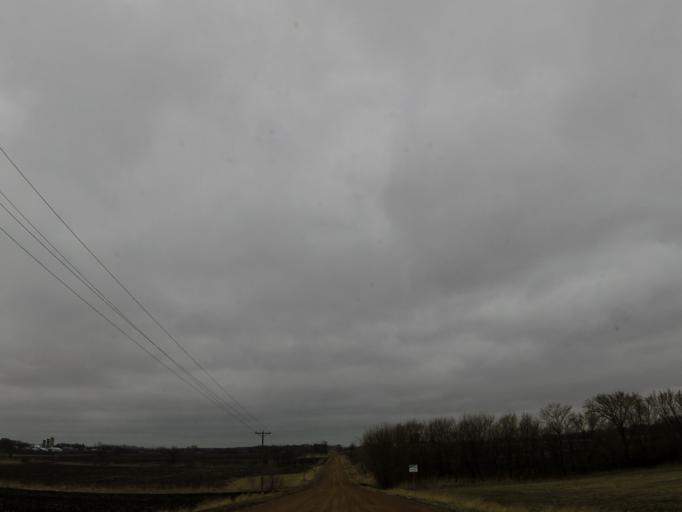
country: US
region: Minnesota
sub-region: Scott County
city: Jordan
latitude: 44.7032
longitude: -93.5411
